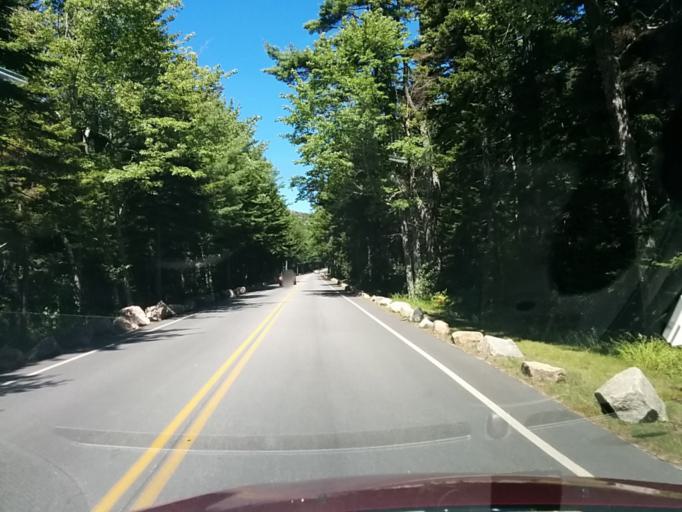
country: US
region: Maine
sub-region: Hancock County
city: Bar Harbor
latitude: 44.3148
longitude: -68.2489
